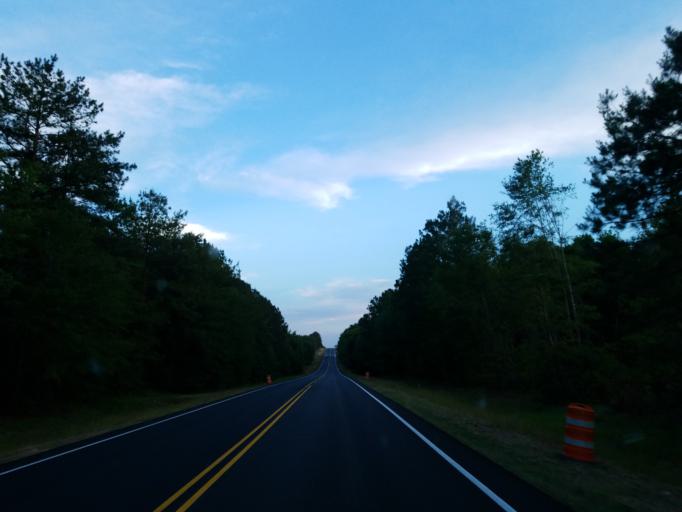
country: US
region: Georgia
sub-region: Turner County
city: Ashburn
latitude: 31.7226
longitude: -83.8082
